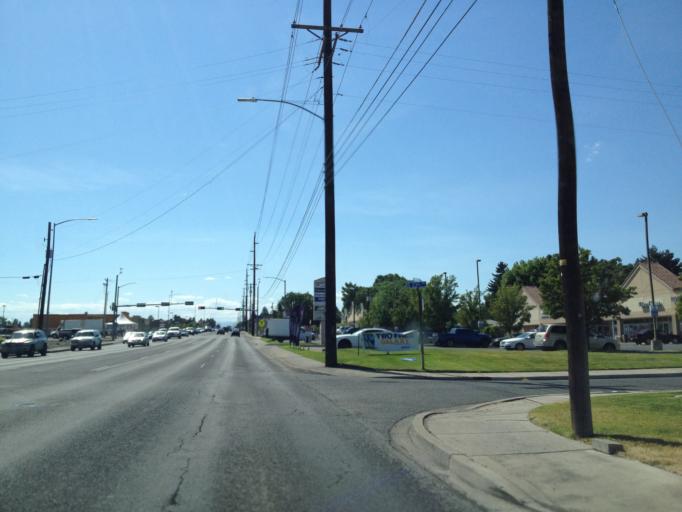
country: US
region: Washington
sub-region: Yakima County
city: Yakima
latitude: 46.5854
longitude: -120.5391
